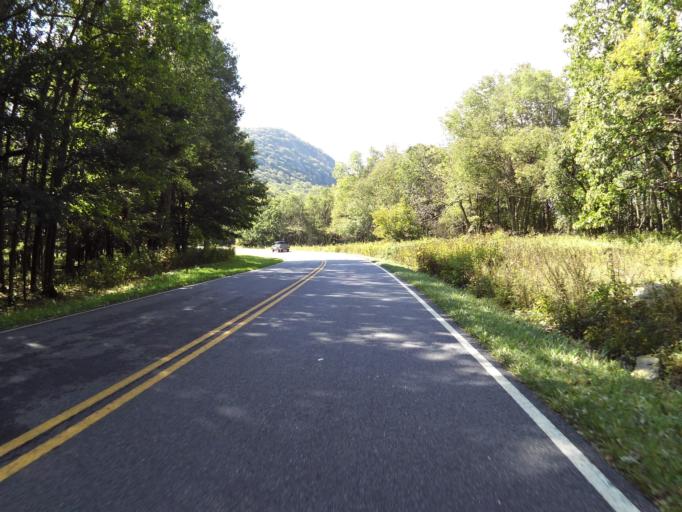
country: US
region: Virginia
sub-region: Page County
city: Stanley
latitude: 38.5570
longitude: -78.3850
